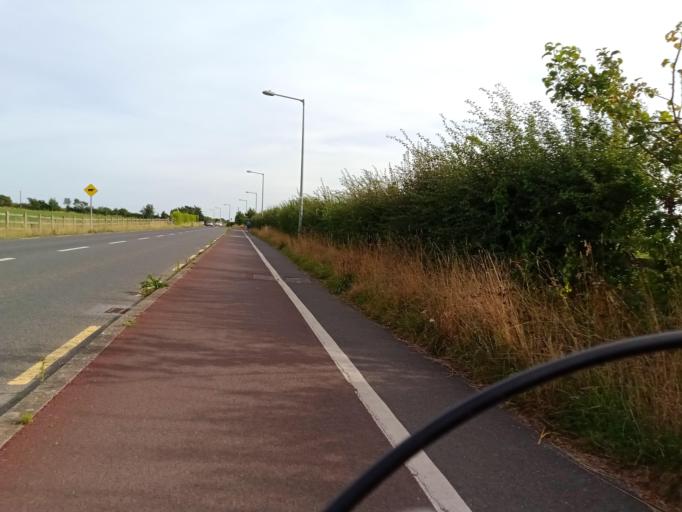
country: IE
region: Munster
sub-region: Waterford
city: Dungarvan
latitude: 52.0964
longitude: -7.5594
